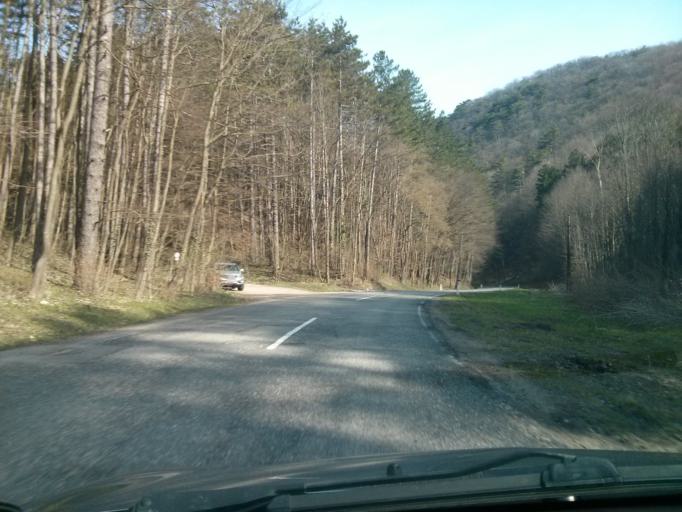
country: AT
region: Lower Austria
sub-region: Politischer Bezirk Baden
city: Hernstein
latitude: 47.9010
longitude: 16.0954
